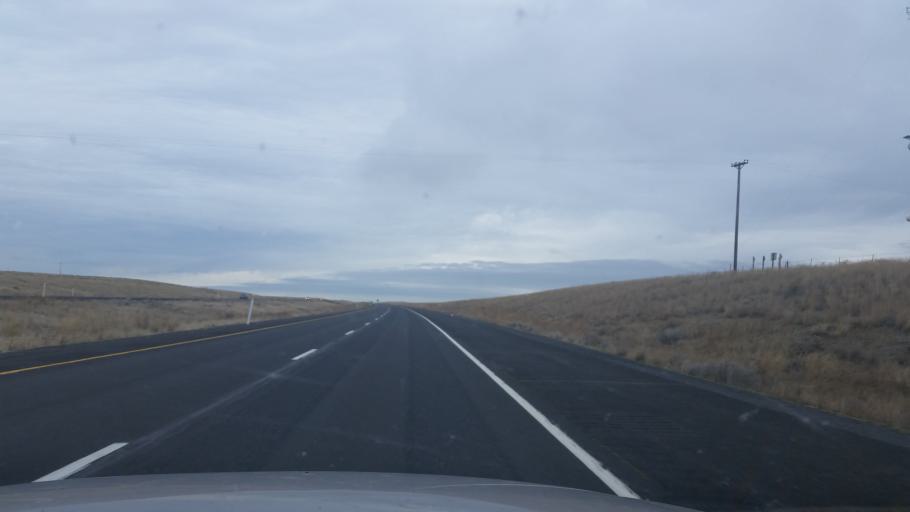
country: US
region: Washington
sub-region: Adams County
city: Ritzville
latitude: 47.1115
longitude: -118.4504
